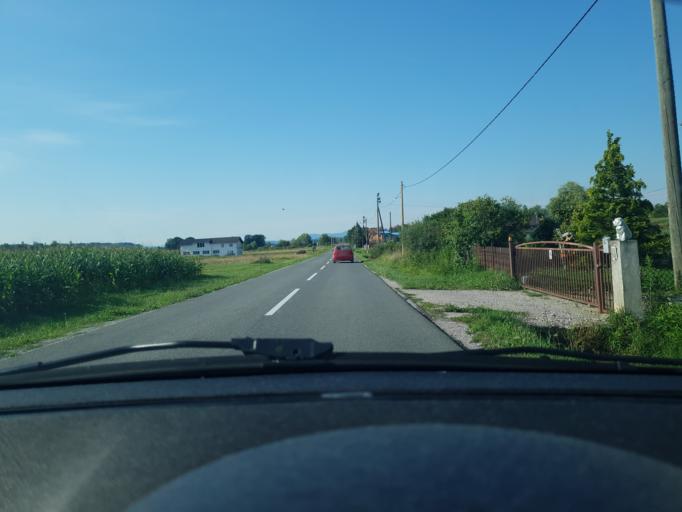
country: HR
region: Zagrebacka
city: Jakovlje
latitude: 45.9612
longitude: 15.8553
